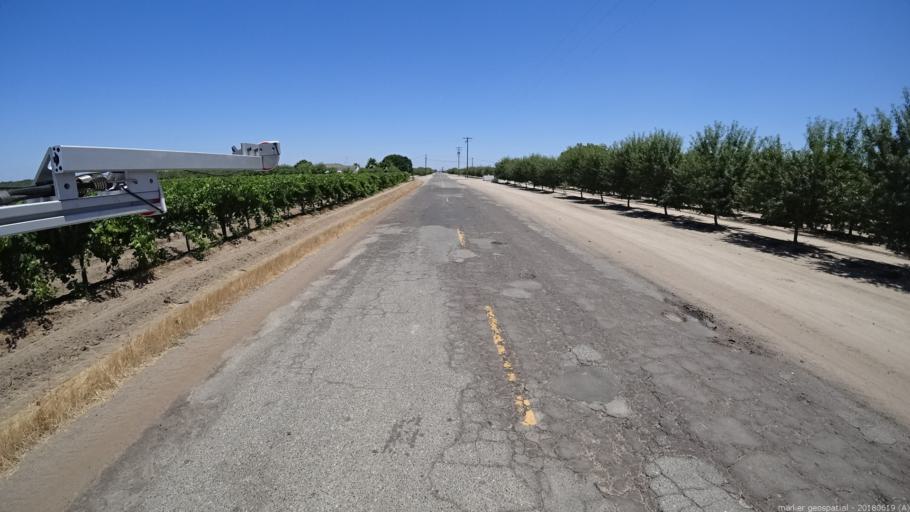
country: US
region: California
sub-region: Madera County
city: Parkwood
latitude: 36.8657
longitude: -120.1204
